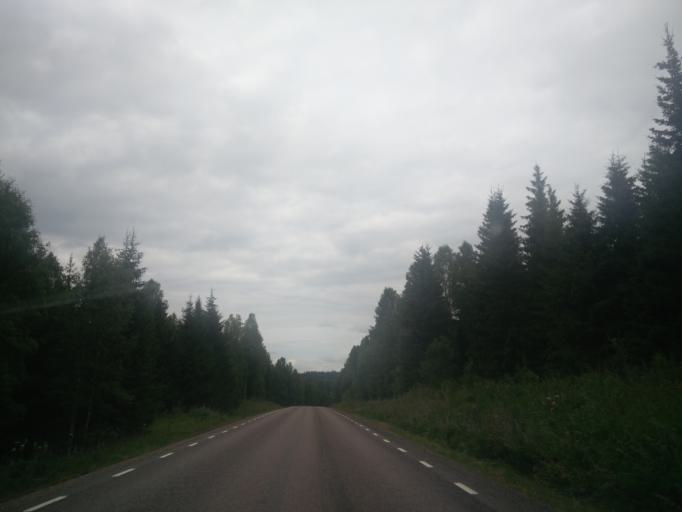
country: SE
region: Vaermland
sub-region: Torsby Kommun
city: Torsby
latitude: 59.9463
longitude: 12.7399
